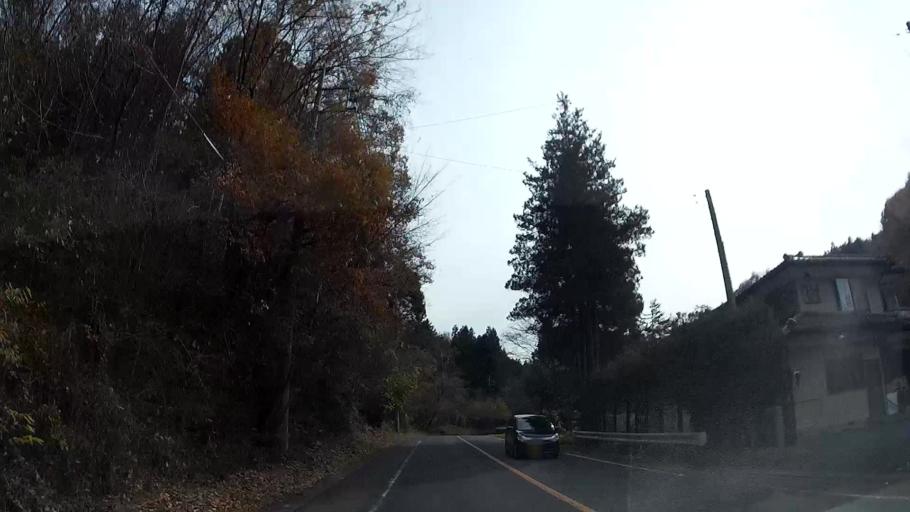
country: JP
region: Saitama
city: Chichibu
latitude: 35.9824
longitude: 139.0383
